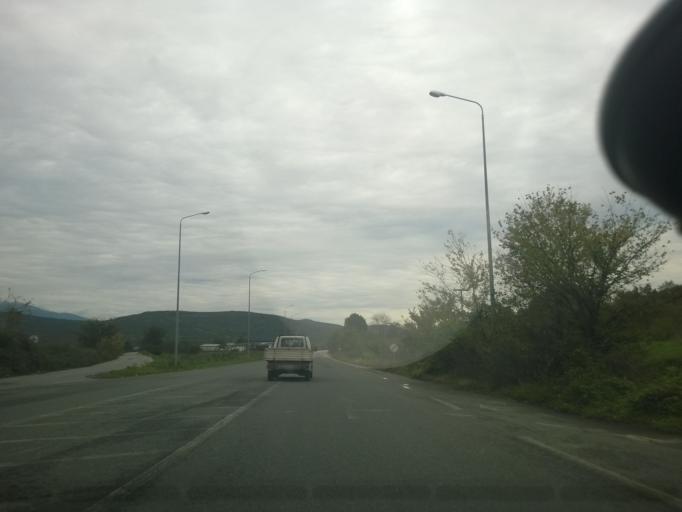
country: GR
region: Central Macedonia
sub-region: Nomos Pellis
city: Apsalos
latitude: 40.8872
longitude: 22.0707
